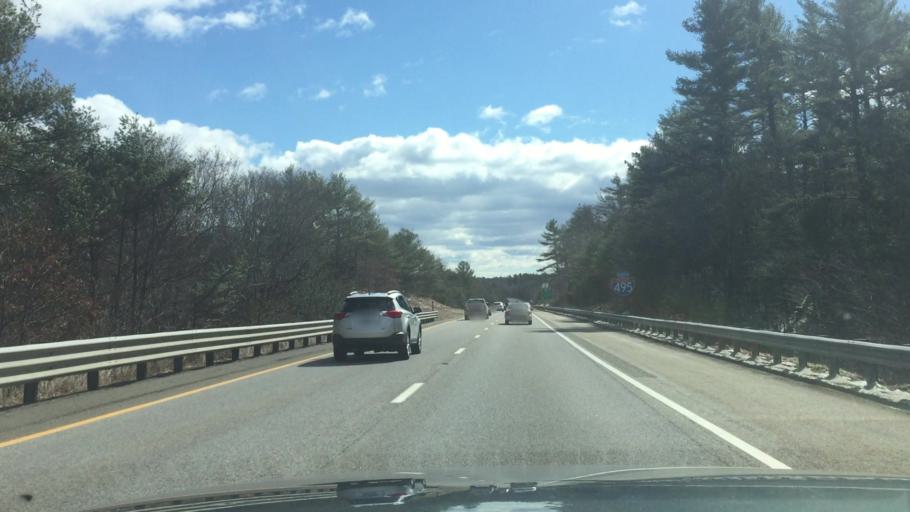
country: US
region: Massachusetts
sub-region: Bristol County
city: Raynham Center
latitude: 41.9283
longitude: -71.0026
